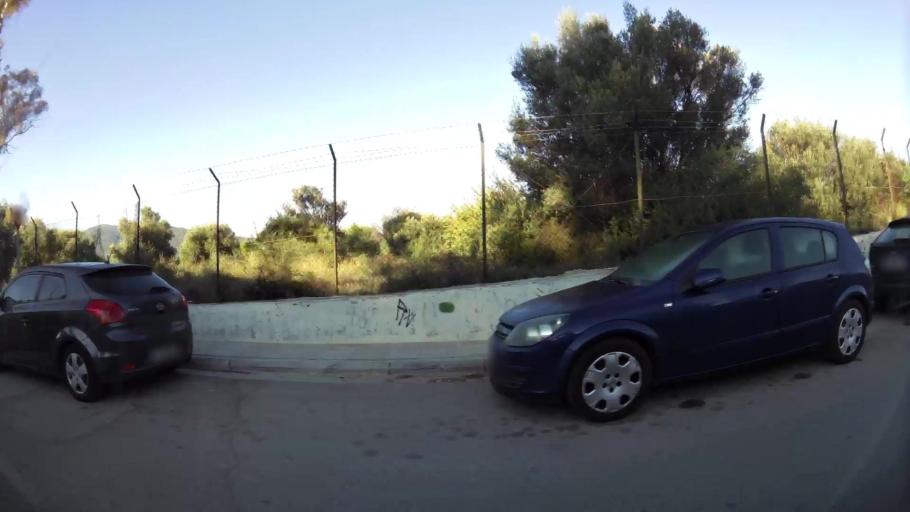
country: GR
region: Attica
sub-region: Nomarchia Anatolikis Attikis
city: Pallini
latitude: 38.0061
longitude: 23.8759
